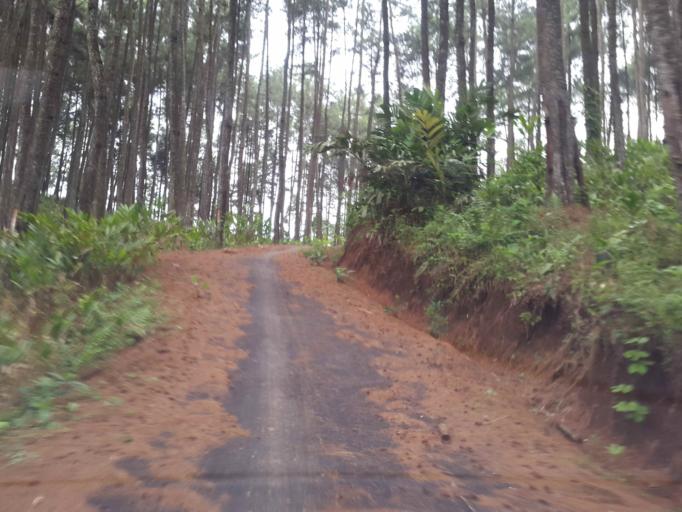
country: ID
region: Central Java
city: Jambuluwuk
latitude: -7.3255
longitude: 108.9548
